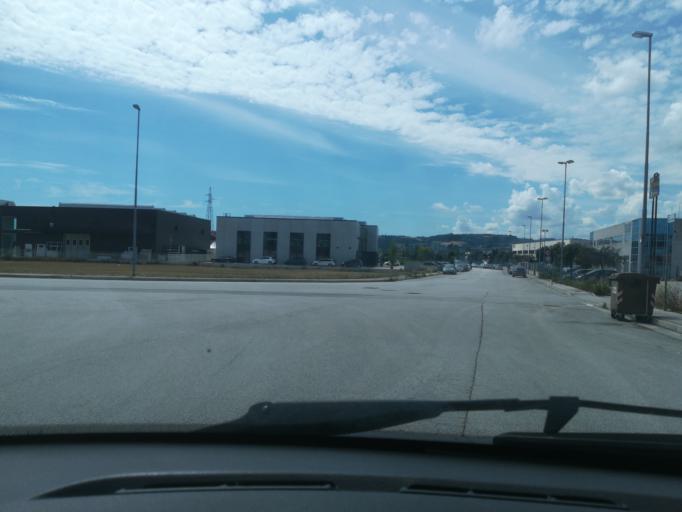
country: IT
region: The Marches
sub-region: Provincia di Macerata
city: Santa Maria Apparente
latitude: 43.2872
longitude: 13.6798
